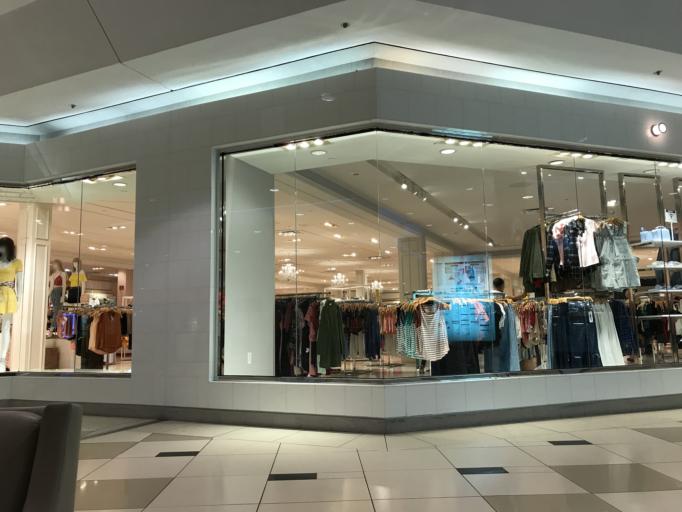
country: US
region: Michigan
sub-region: Oakland County
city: Novi
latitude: 42.4918
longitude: -83.4707
